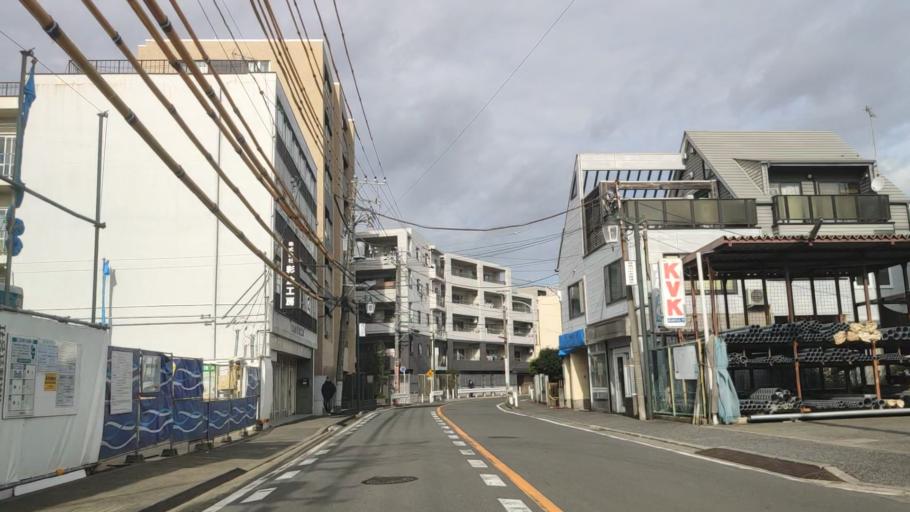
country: JP
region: Kanagawa
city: Yokohama
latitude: 35.4812
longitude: 139.6272
